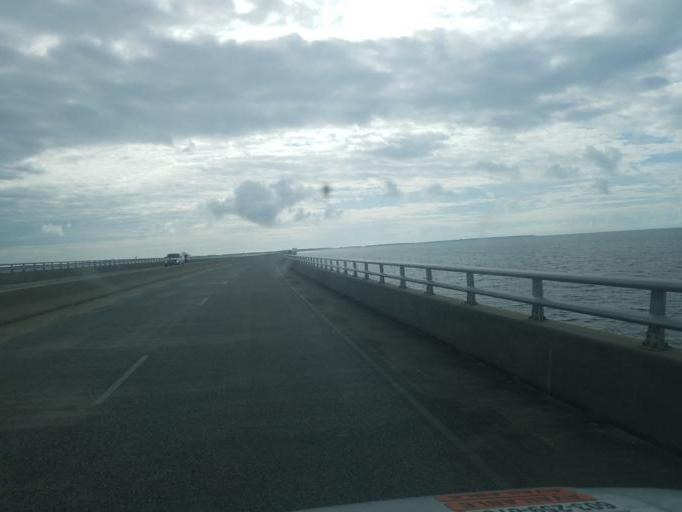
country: US
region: North Carolina
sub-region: Dare County
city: Manteo
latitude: 35.8885
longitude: -75.7491
